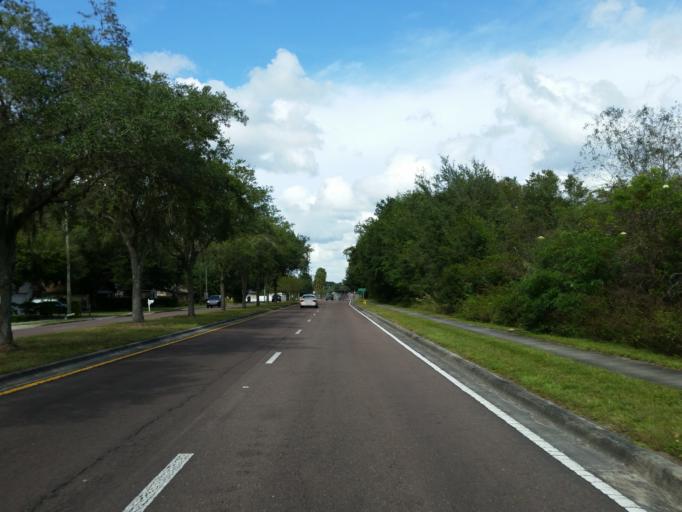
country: US
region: Florida
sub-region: Hillsborough County
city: Brandon
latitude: 27.9180
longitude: -82.2938
